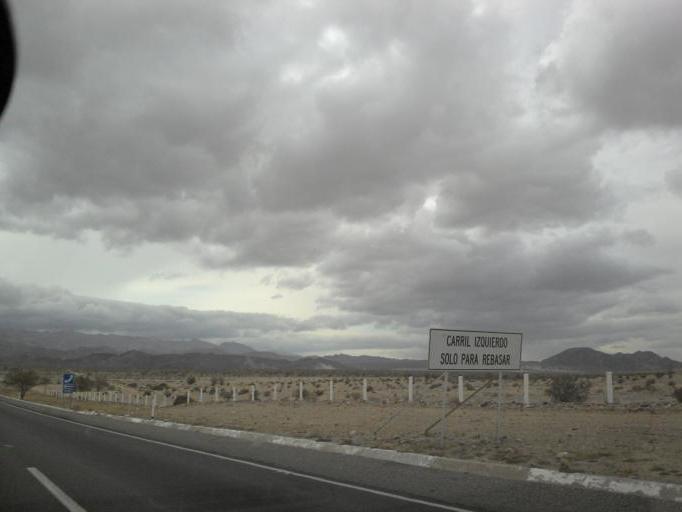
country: MX
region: Baja California
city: Progreso
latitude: 32.5647
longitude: -115.8779
